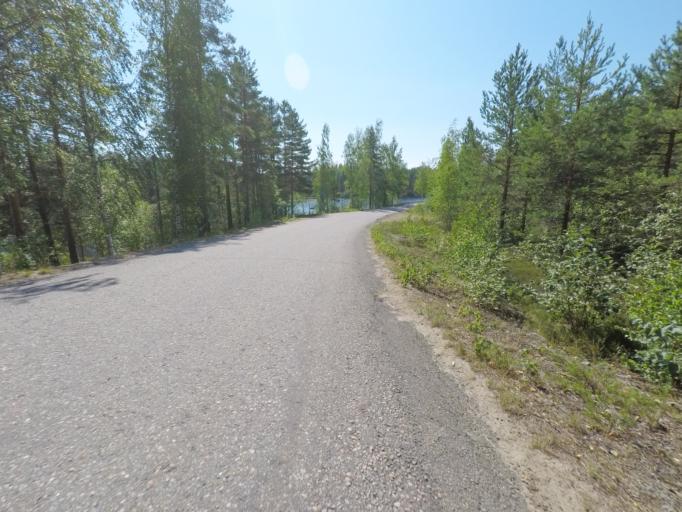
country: FI
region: Southern Savonia
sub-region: Mikkeli
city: Puumala
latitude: 61.4107
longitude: 28.0926
